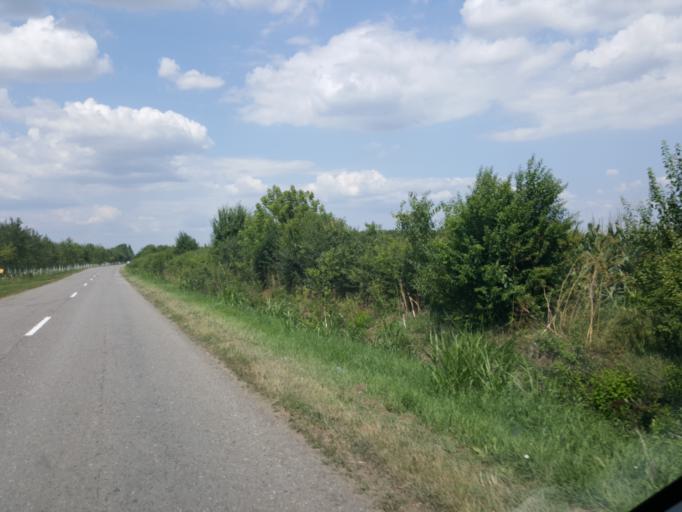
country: RS
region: Autonomna Pokrajina Vojvodina
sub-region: Sremski Okrug
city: Pecinci
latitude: 44.8561
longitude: 19.9607
